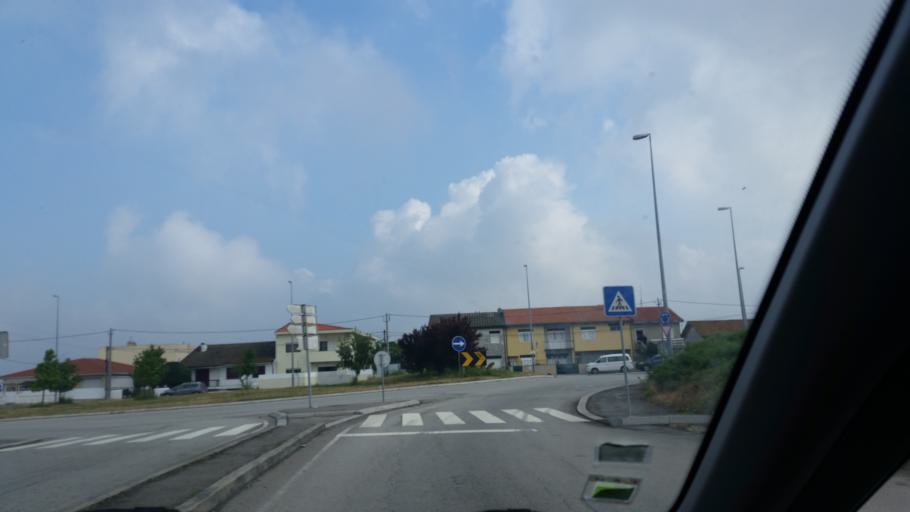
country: PT
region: Porto
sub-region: Matosinhos
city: Guifoes
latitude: 41.2040
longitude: -8.6539
